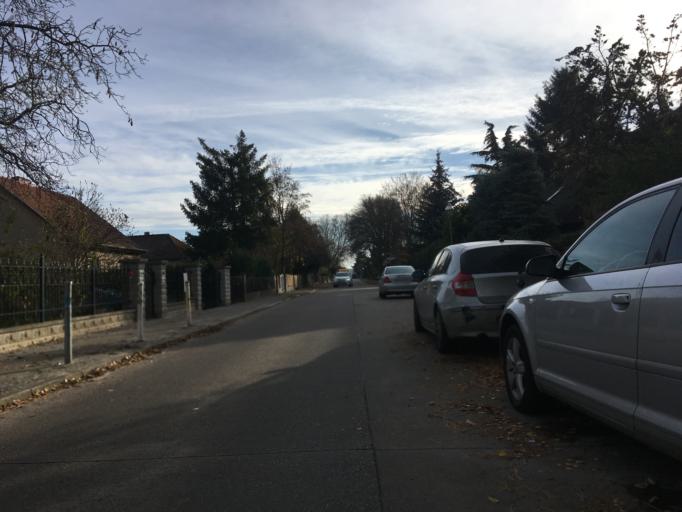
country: DE
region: Berlin
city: Rudow
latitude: 52.4344
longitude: 13.4838
